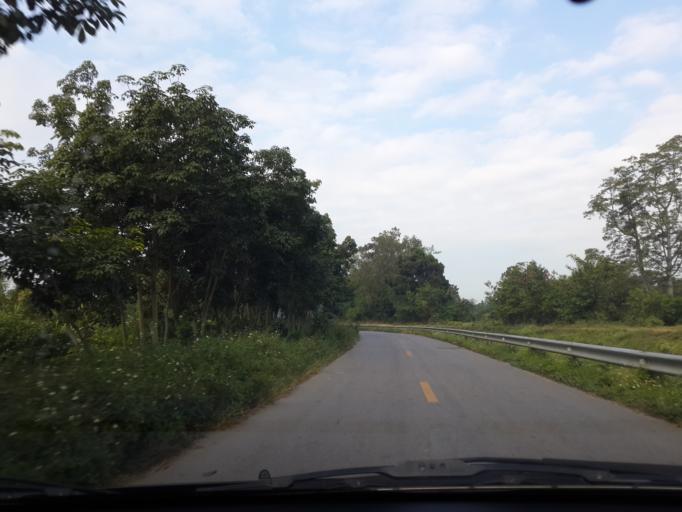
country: TH
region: Chiang Mai
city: San Sai
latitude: 18.9003
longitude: 99.0461
